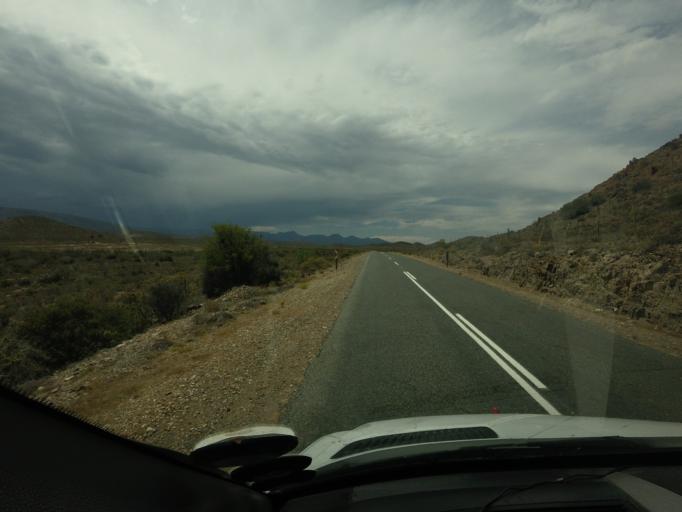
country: ZA
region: Western Cape
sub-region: Eden District Municipality
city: Ladismith
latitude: -33.6281
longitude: 21.0491
